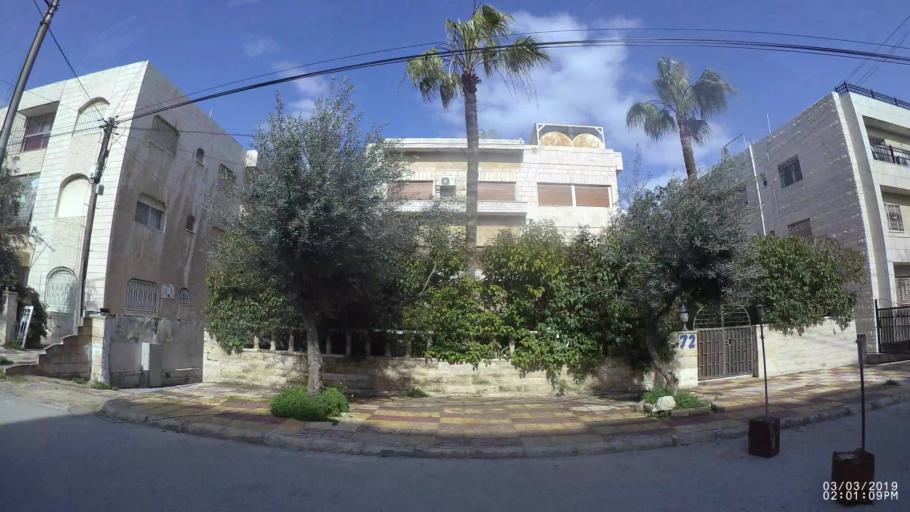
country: JO
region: Amman
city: Al Jubayhah
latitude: 31.9789
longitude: 35.8934
